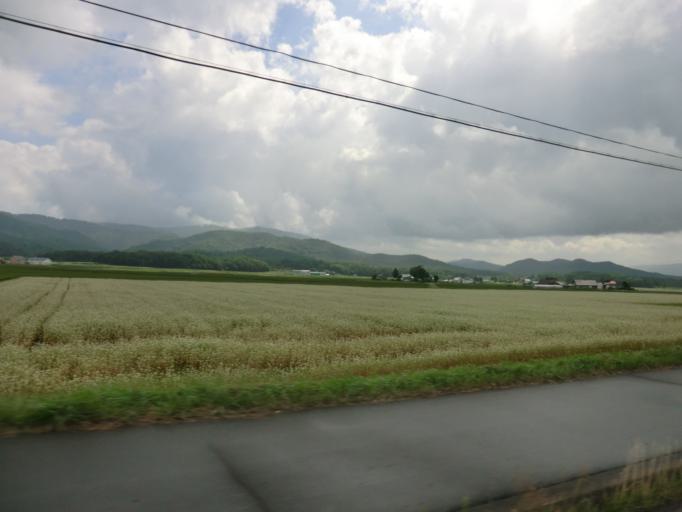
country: JP
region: Hokkaido
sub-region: Asahikawa-shi
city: Asahikawa
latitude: 44.0277
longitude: 142.1515
